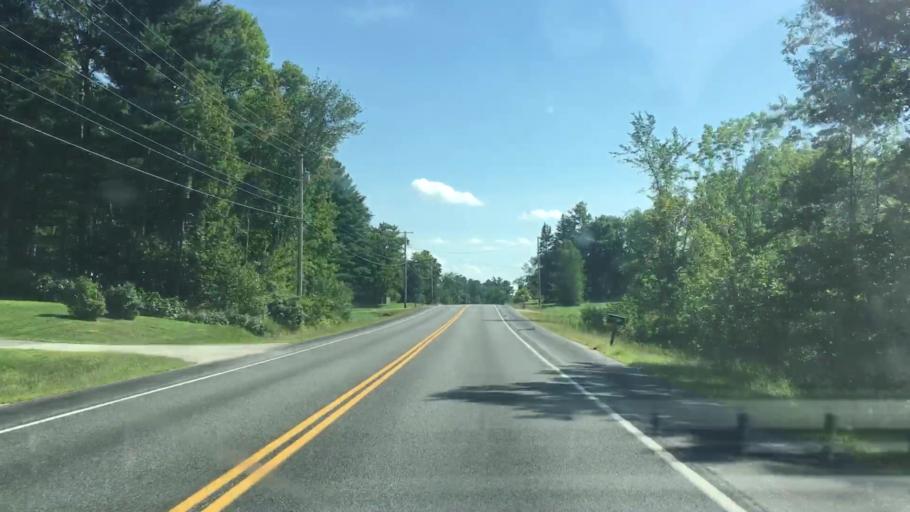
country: US
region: Maine
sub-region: Androscoggin County
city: Sabattus
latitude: 44.0790
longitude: -70.0794
